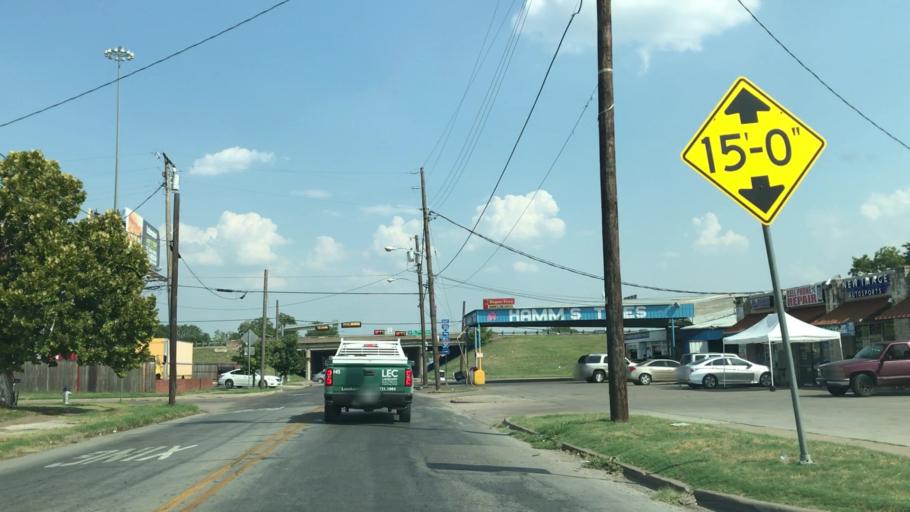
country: US
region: Texas
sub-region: Dallas County
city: Dallas
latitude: 32.7898
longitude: -96.7655
